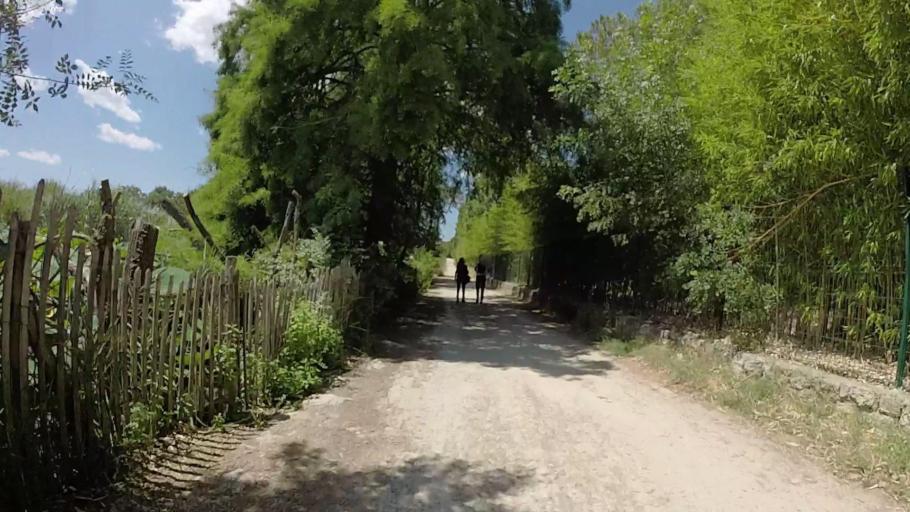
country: FR
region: Provence-Alpes-Cote d'Azur
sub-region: Departement des Alpes-Maritimes
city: Mougins
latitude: 43.5989
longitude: 7.0119
